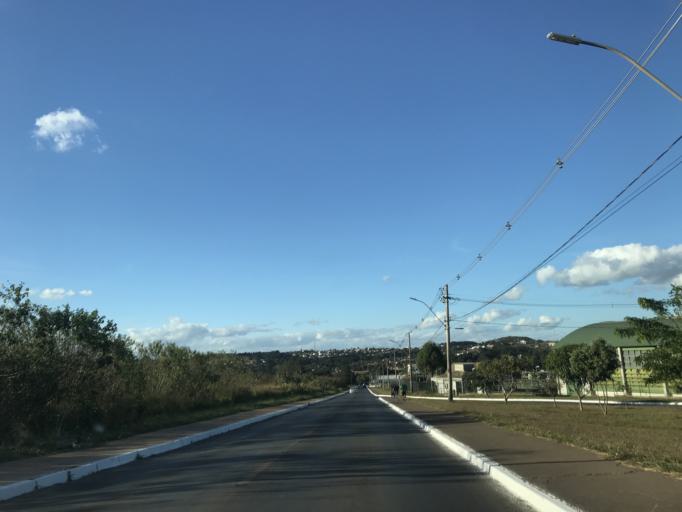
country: BR
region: Federal District
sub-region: Brasilia
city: Brasilia
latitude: -15.8921
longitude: -47.7830
